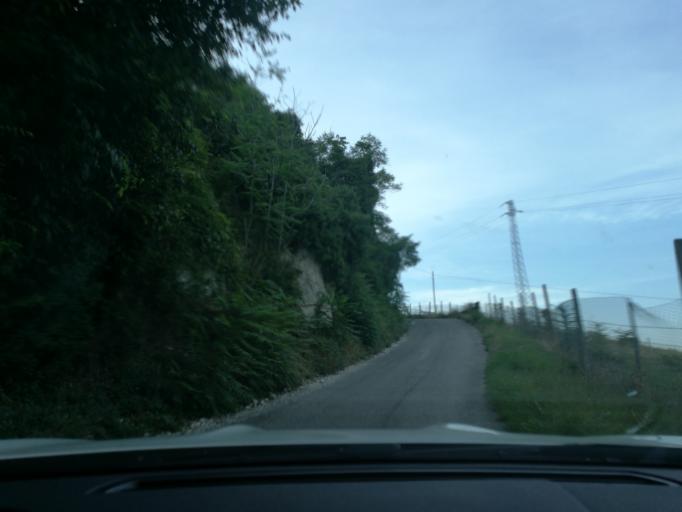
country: IT
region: Umbria
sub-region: Provincia di Terni
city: San Gemini
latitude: 42.6143
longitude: 12.5492
